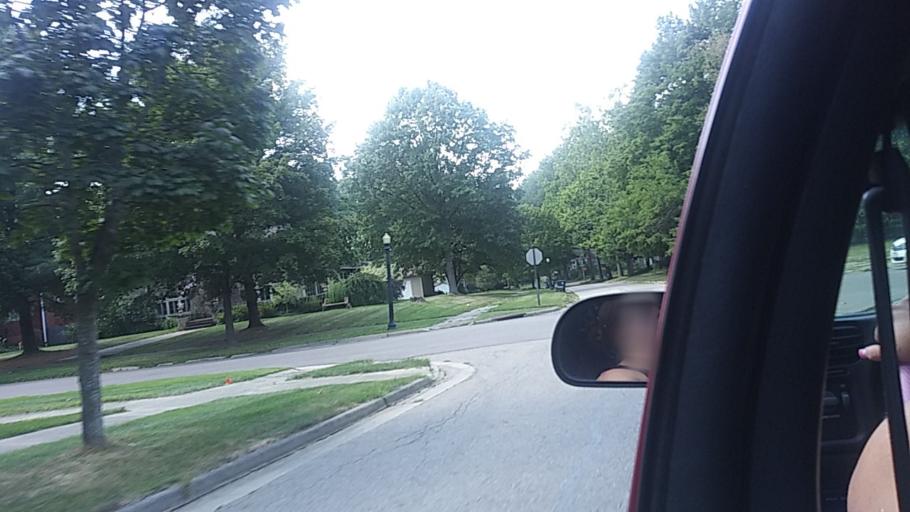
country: US
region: Ohio
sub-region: Summit County
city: Akron
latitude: 41.0964
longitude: -81.5586
